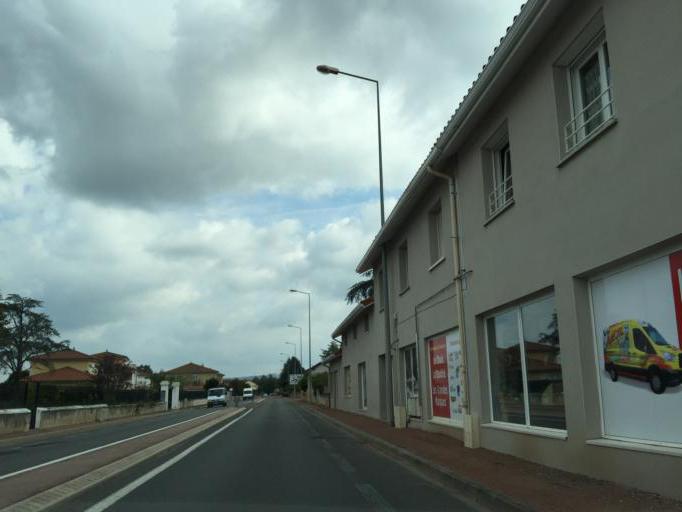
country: FR
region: Rhone-Alpes
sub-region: Departement de la Loire
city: Bonson
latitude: 45.5249
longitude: 4.2114
